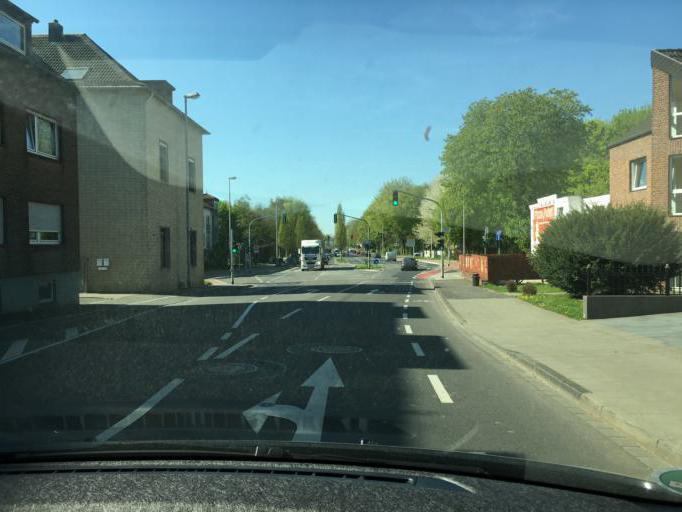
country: DE
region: North Rhine-Westphalia
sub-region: Regierungsbezirk Dusseldorf
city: Monchengladbach
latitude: 51.1503
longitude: 6.4331
